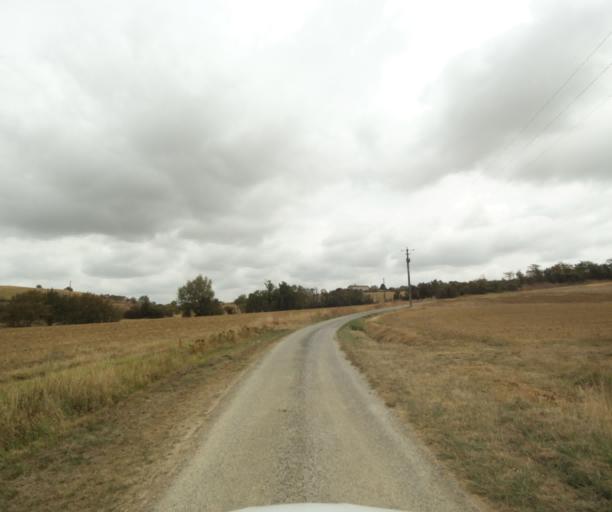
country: FR
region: Midi-Pyrenees
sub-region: Departement de la Haute-Garonne
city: Villefranche-de-Lauragais
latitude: 43.4173
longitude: 1.7321
